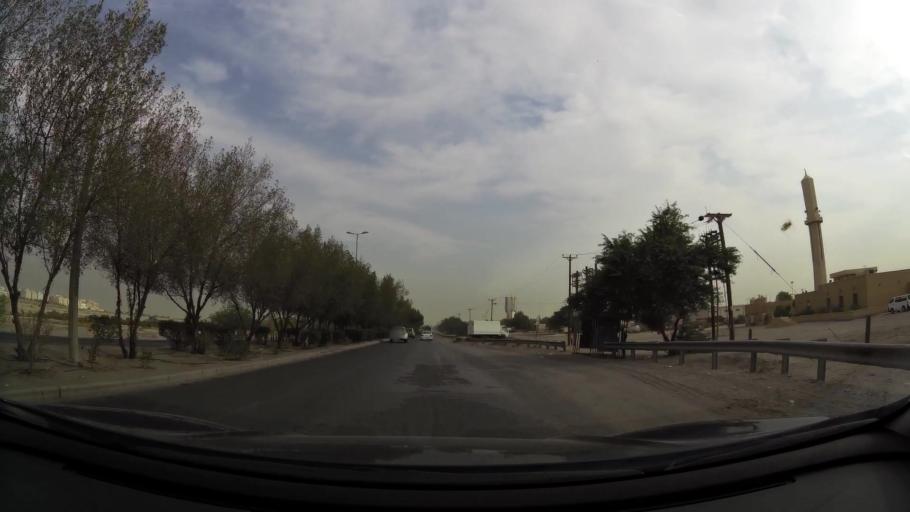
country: KW
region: Muhafazat al Jahra'
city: Al Jahra'
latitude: 29.3164
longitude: 47.7469
